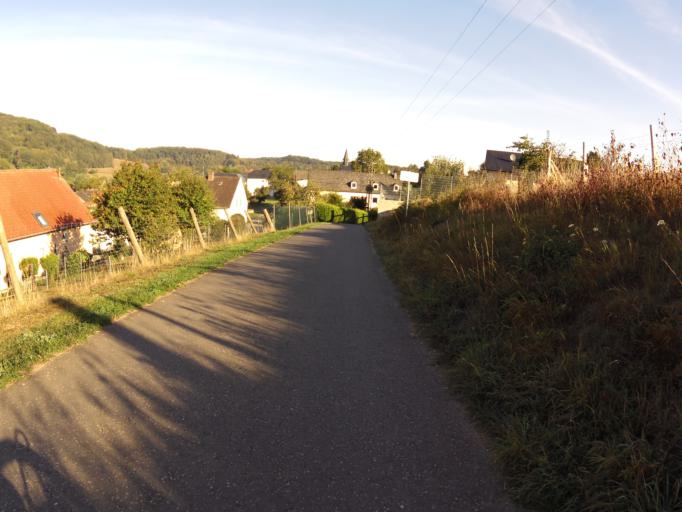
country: DE
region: Rheinland-Pfalz
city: Peffingen
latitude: 49.9065
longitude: 6.4106
